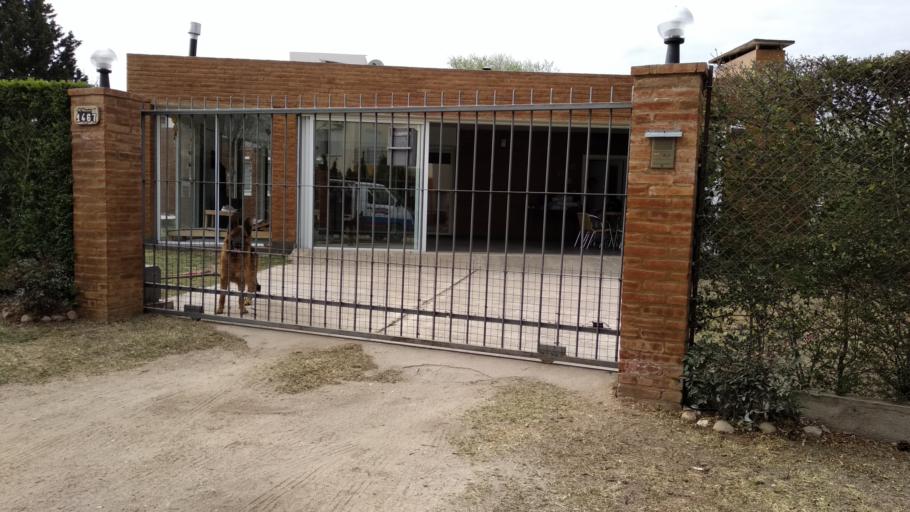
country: AR
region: Cordoba
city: Mina Clavero
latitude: -31.7327
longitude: -65.0140
